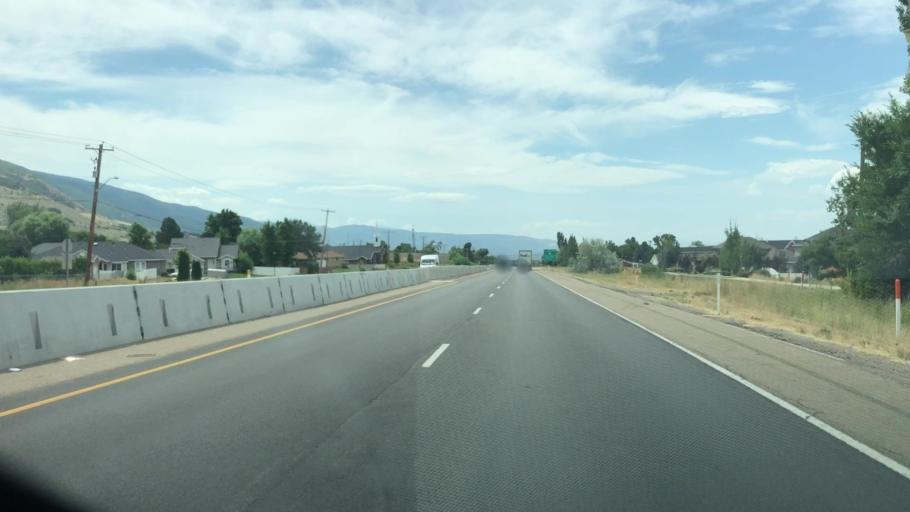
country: US
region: Utah
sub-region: Davis County
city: Fruit Heights
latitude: 41.0364
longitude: -111.9093
